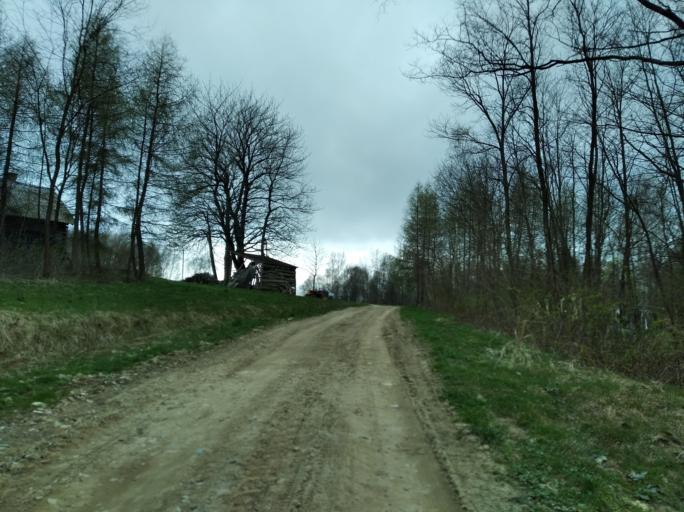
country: PL
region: Subcarpathian Voivodeship
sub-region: Powiat strzyzowski
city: Jawornik
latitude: 49.8207
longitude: 21.8941
